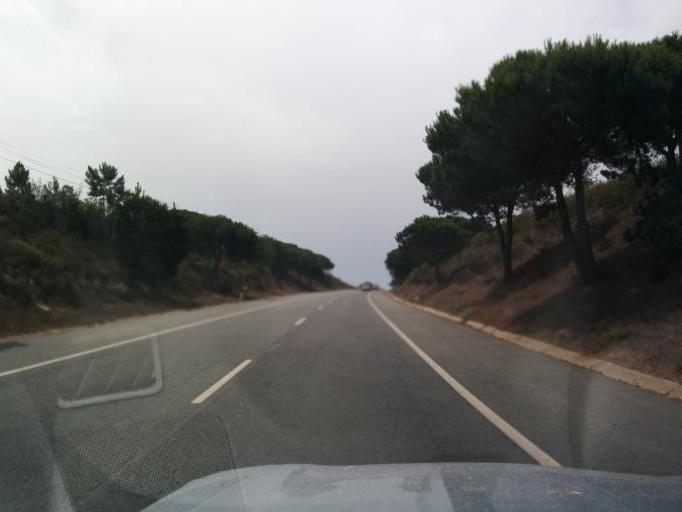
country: PT
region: Beja
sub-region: Odemira
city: Vila Nova de Milfontes
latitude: 37.7199
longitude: -8.7669
